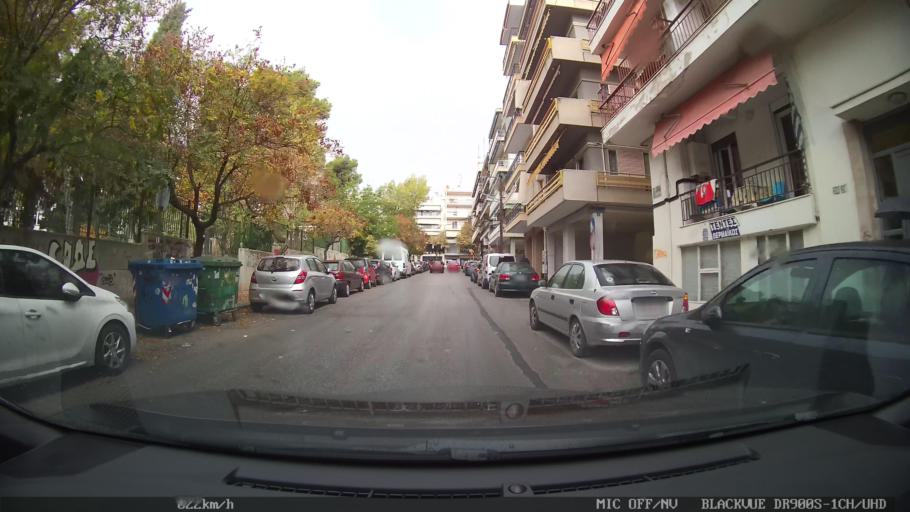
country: GR
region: Central Macedonia
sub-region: Nomos Thessalonikis
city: Triandria
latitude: 40.6124
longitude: 22.9809
